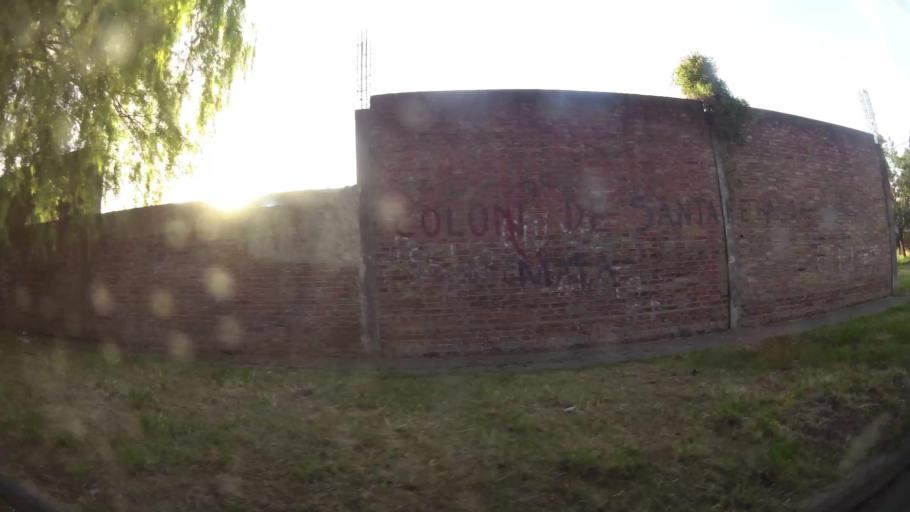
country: AR
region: Santa Fe
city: Santa Fe de la Vera Cruz
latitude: -31.5990
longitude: -60.6854
